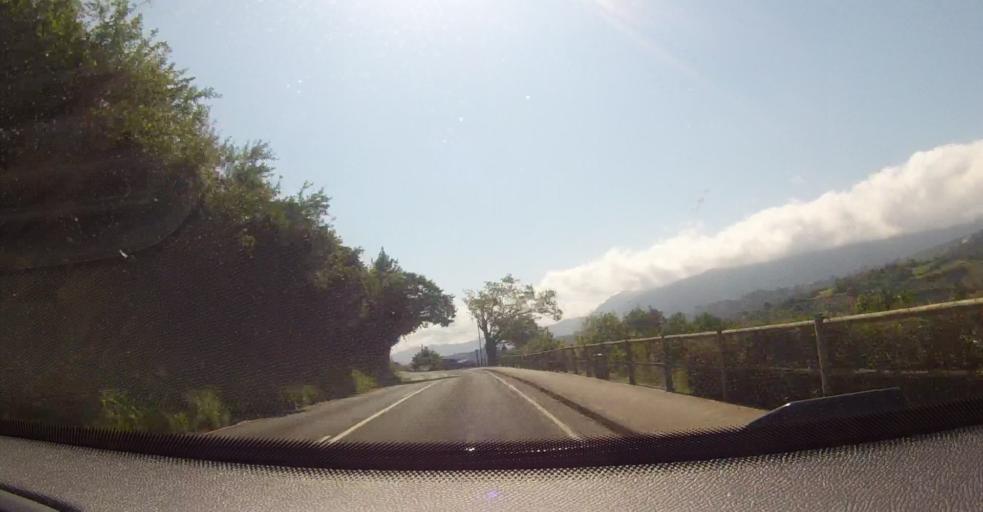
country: ES
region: Asturias
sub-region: Province of Asturias
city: Colunga
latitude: 43.4877
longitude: -5.2916
